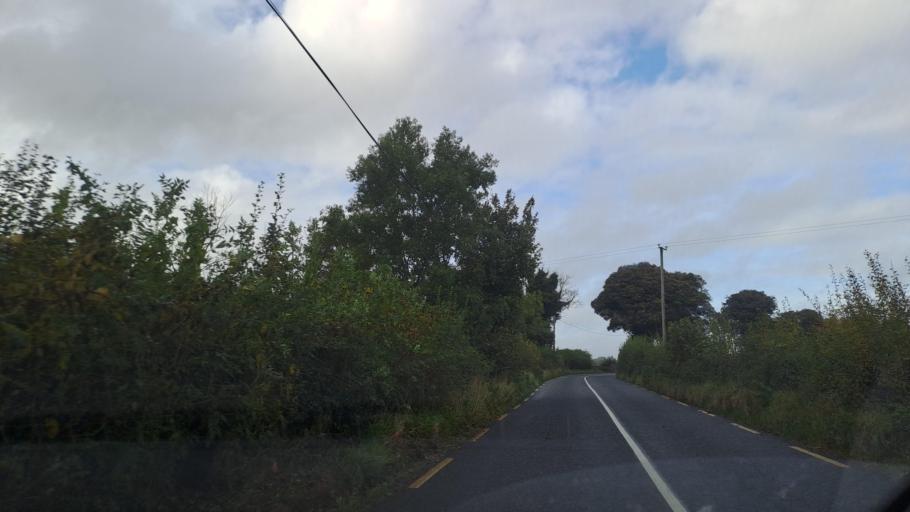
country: IE
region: Ulster
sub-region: County Monaghan
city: Carrickmacross
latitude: 53.9183
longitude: -6.7113
